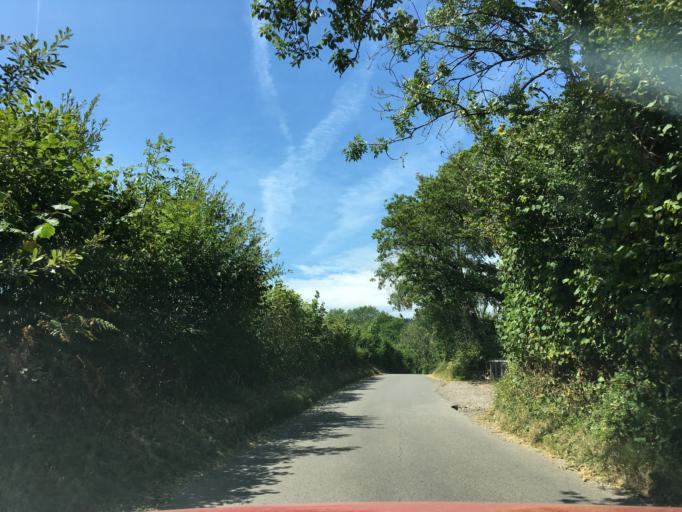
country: GB
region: Wales
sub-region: Caerphilly County Borough
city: Machen
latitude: 51.5562
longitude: -3.1453
